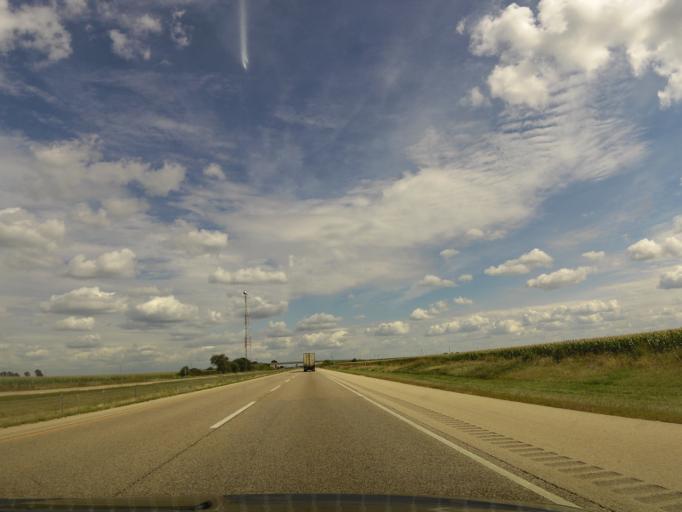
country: US
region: Illinois
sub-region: Ogle County
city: Rochelle
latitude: 41.9038
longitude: -88.9671
